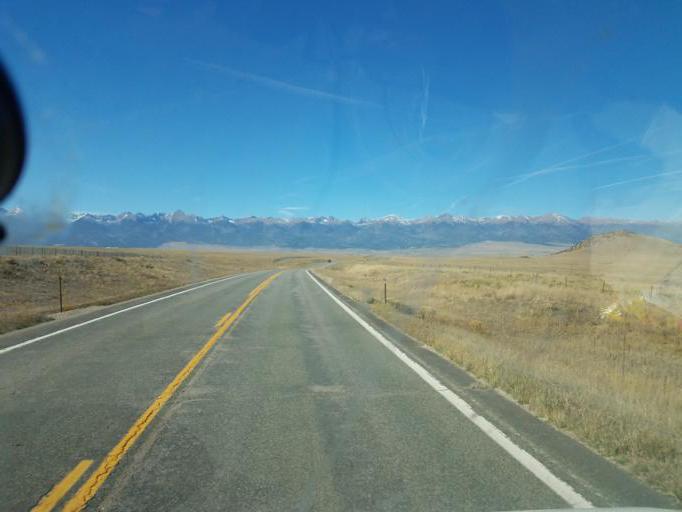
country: US
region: Colorado
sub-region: Custer County
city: Westcliffe
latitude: 38.1384
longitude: -105.3844
